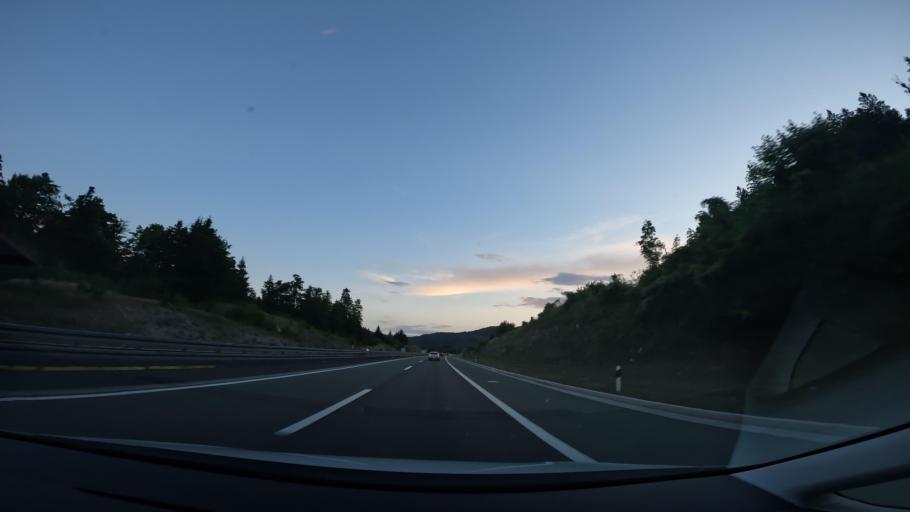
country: HR
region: Primorsko-Goranska
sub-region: Grad Delnice
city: Delnice
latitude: 45.3678
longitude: 14.7609
